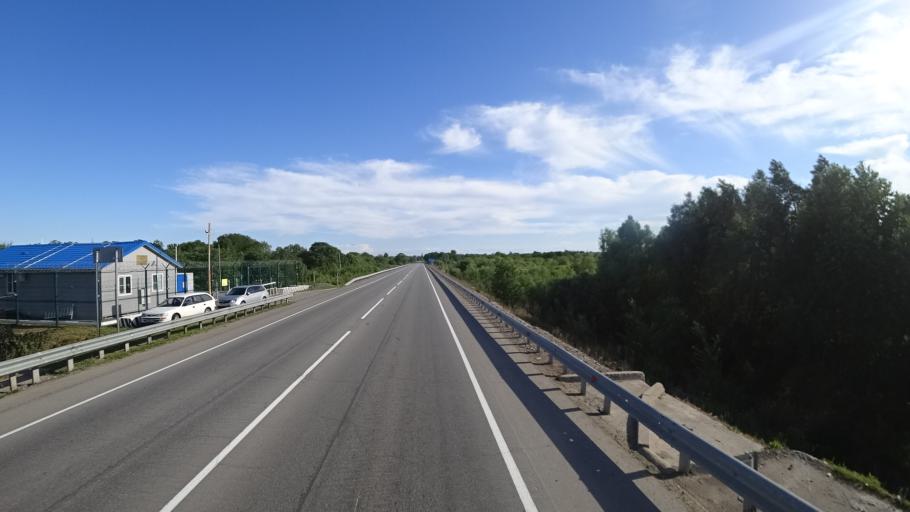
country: RU
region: Khabarovsk Krai
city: Khor
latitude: 47.8632
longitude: 134.9635
